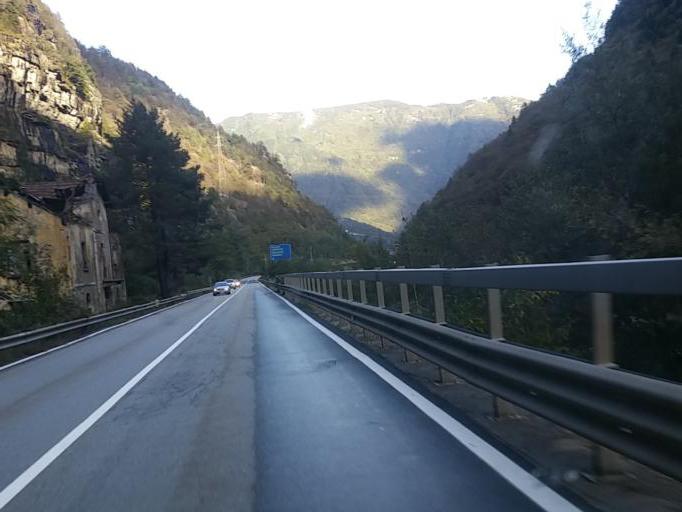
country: IT
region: Piedmont
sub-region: Provincia Verbano-Cusio-Ossola
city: Trasquera
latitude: 46.2055
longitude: 8.2154
